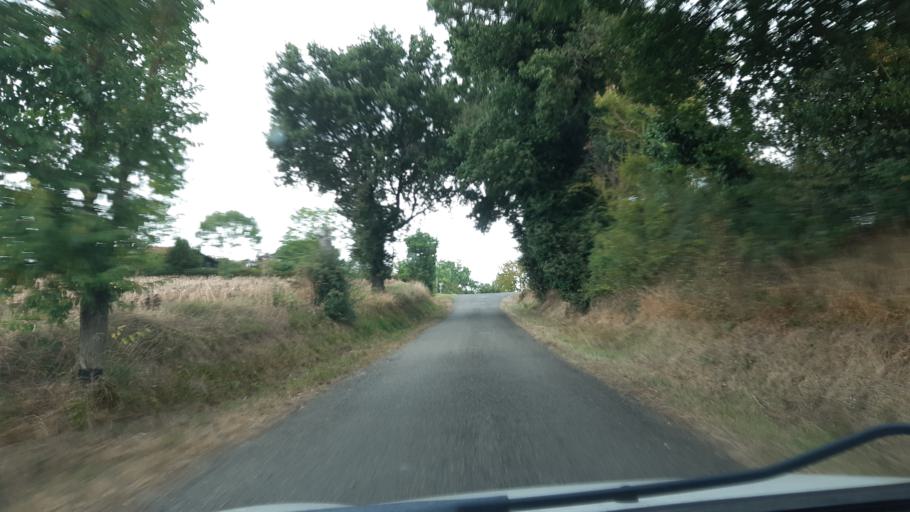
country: FR
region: Midi-Pyrenees
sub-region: Departement du Gers
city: Gimont
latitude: 43.6781
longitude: 0.9933
